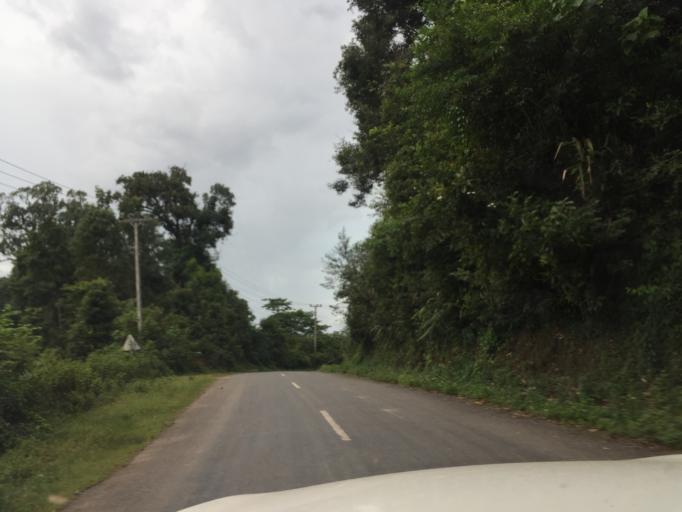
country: LA
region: Phongsali
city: Phongsali
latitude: 21.3230
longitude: 102.0486
